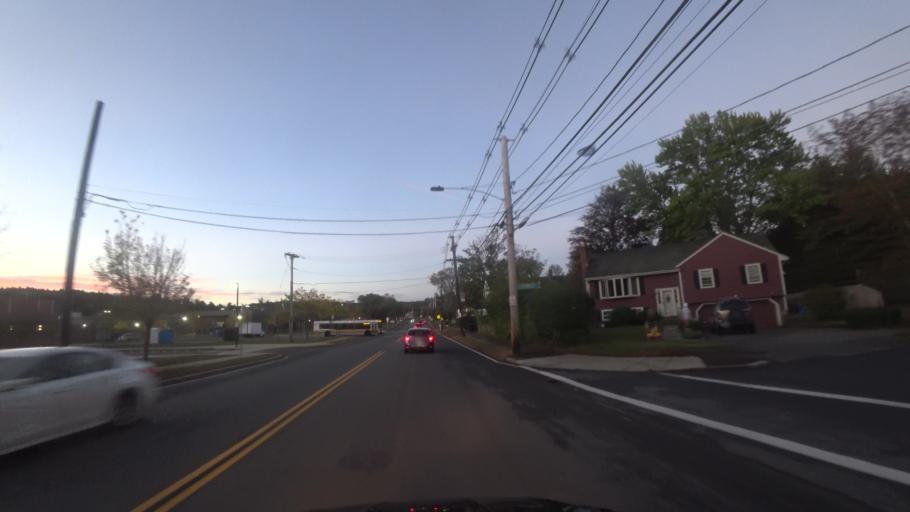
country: US
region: Massachusetts
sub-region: Middlesex County
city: Wakefield
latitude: 42.4985
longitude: -71.0512
